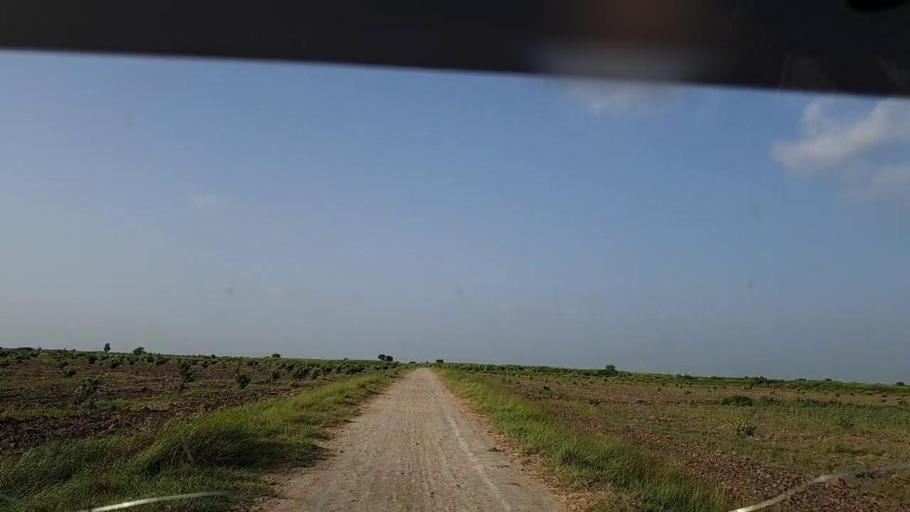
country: PK
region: Sindh
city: Badin
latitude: 24.5641
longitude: 68.8826
